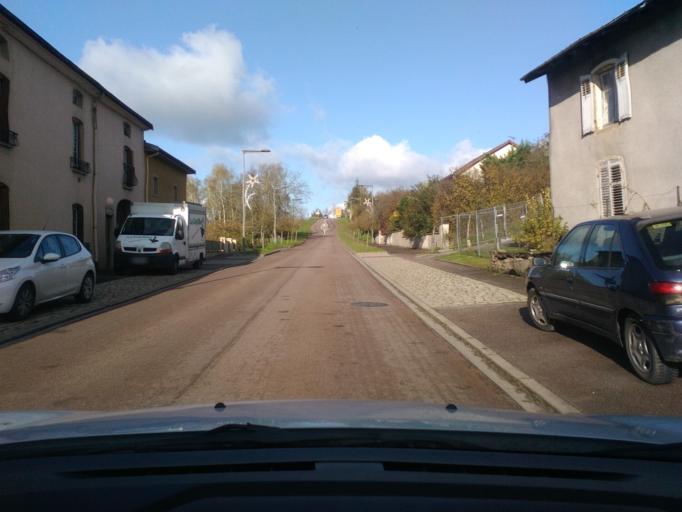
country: FR
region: Lorraine
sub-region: Departement des Vosges
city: Mirecourt
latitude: 48.3241
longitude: 6.1268
